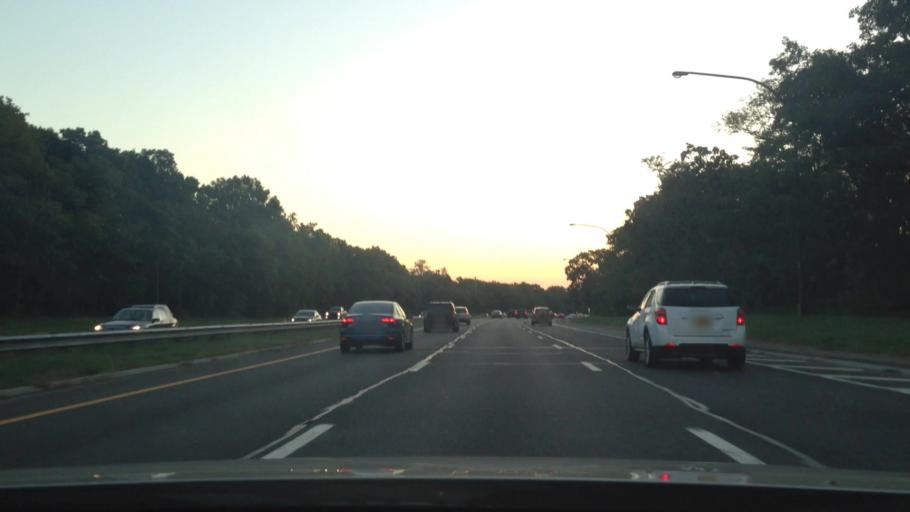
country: US
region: New York
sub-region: Nassau County
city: North Massapequa
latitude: 40.7043
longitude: -73.4760
